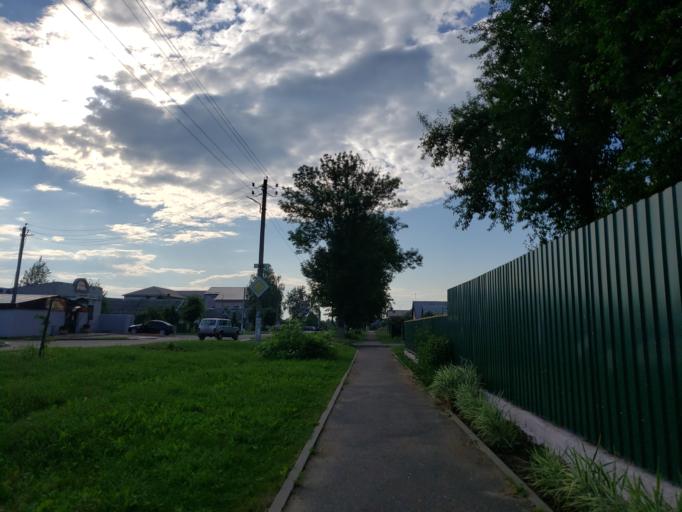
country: BY
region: Minsk
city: Chervyen'
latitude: 53.7048
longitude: 28.4372
